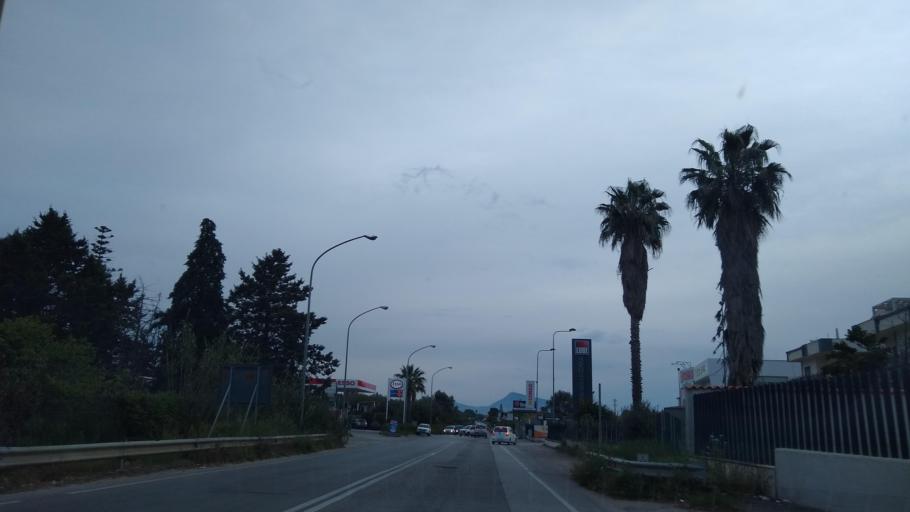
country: IT
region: Sicily
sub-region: Palermo
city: Partinico
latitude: 38.0381
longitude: 13.1051
